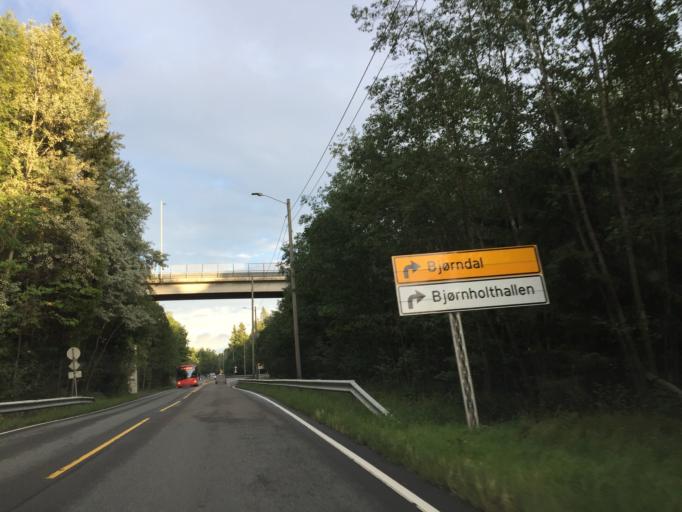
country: NO
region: Akershus
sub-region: Oppegard
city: Kolbotn
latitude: 59.8382
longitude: 10.8330
